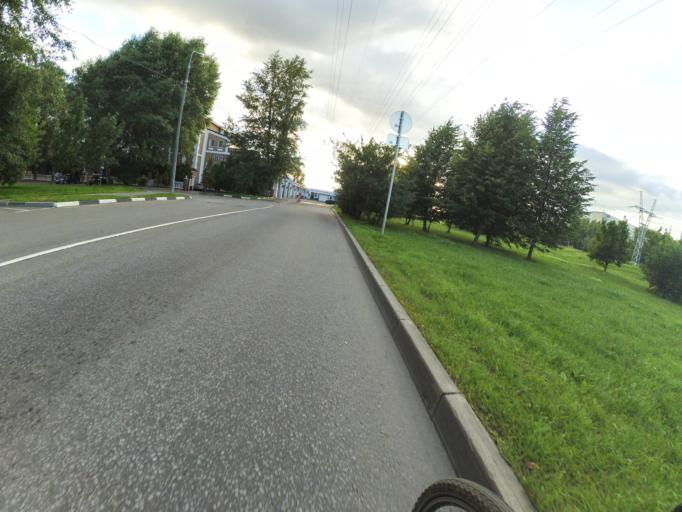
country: RU
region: Moscow
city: Pokrovskoye-Streshnevo
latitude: 55.8352
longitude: 37.4484
